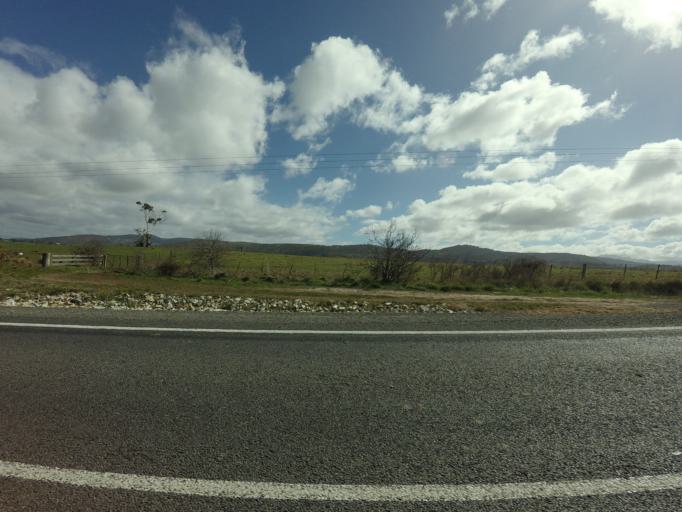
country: AU
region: Tasmania
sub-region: Northern Midlands
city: Evandale
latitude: -41.8038
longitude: 147.6840
